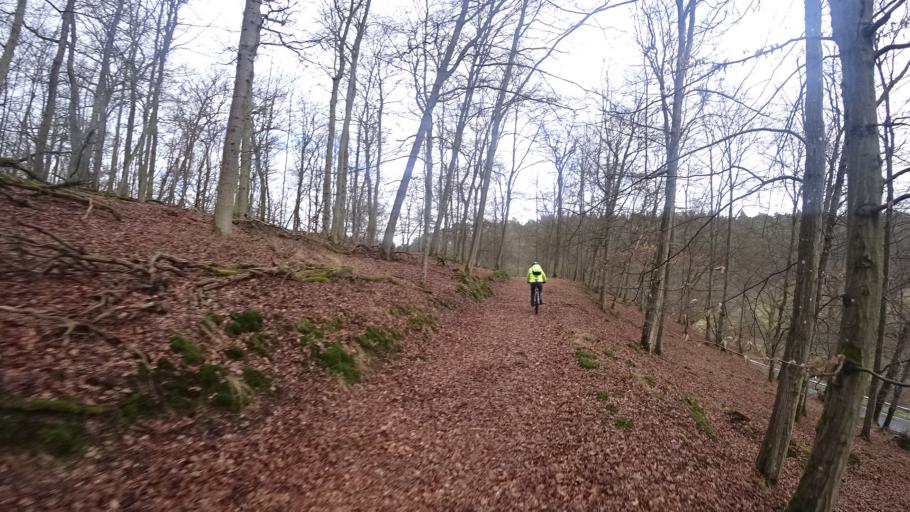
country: DE
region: Rheinland-Pfalz
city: Diethardt
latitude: 50.1724
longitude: 7.8698
